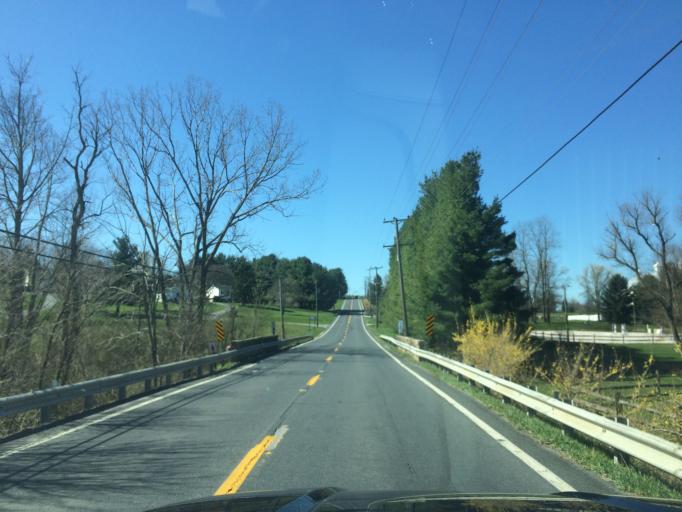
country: US
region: Maryland
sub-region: Carroll County
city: Manchester
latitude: 39.6614
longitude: -76.9480
